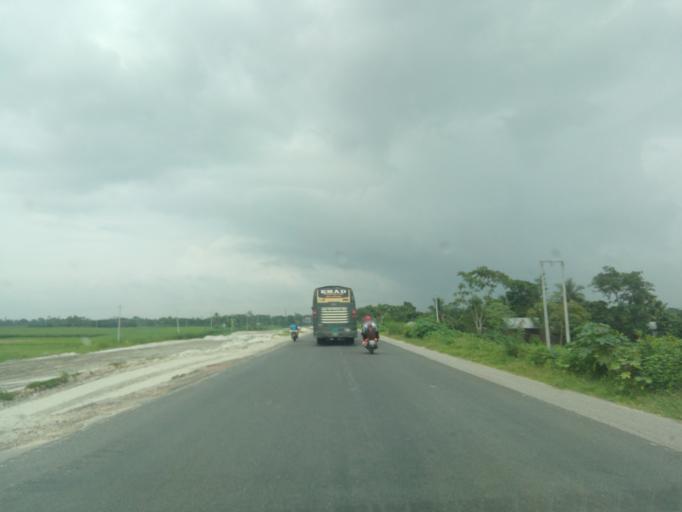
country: BD
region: Dhaka
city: Char Bhadrasan
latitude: 23.3699
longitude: 90.0541
